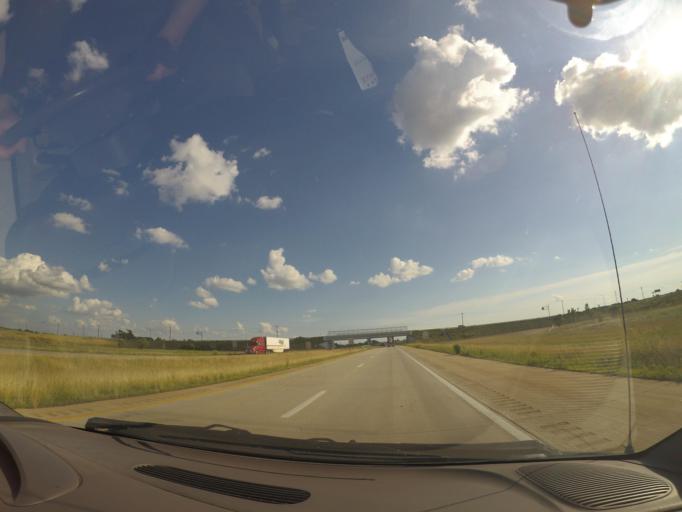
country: US
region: Ohio
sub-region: Lucas County
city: Waterville
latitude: 41.5102
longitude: -83.7534
